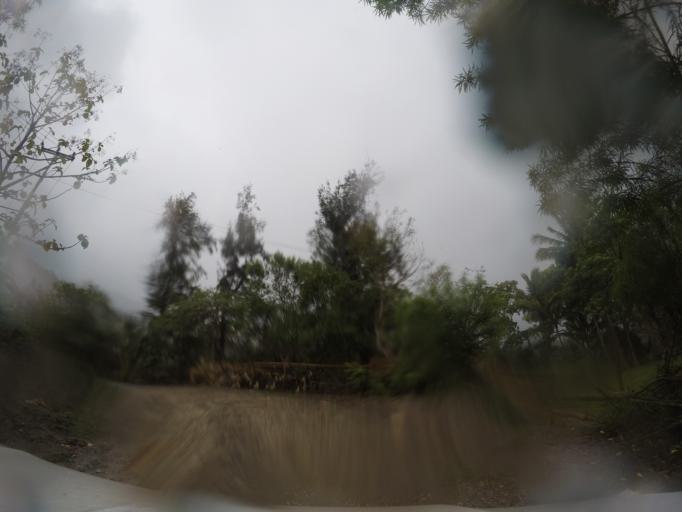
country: TL
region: Baucau
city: Venilale
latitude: -8.6410
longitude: 126.4377
